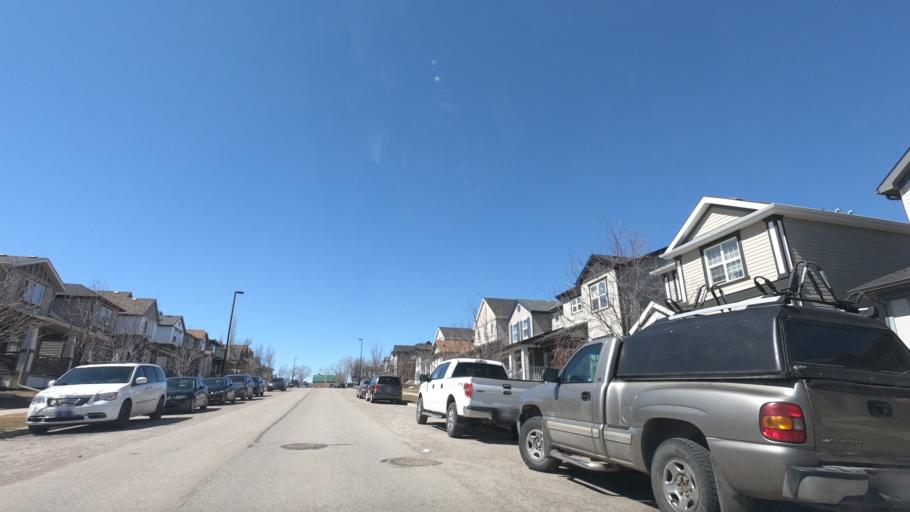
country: CA
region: Alberta
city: Airdrie
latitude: 51.3048
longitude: -114.0450
